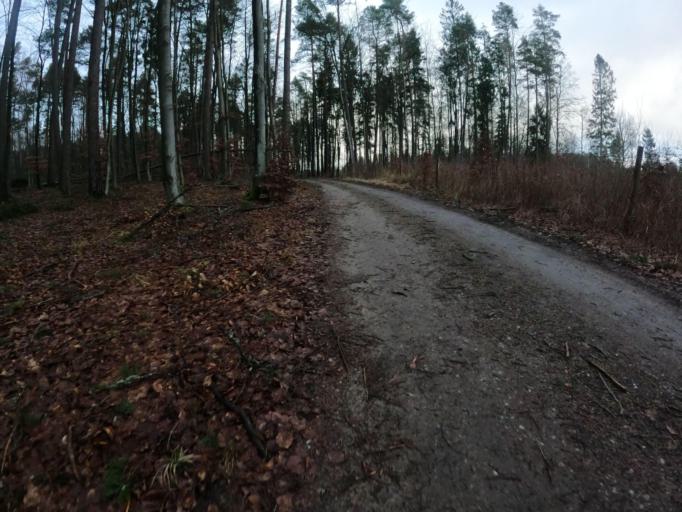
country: PL
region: West Pomeranian Voivodeship
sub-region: Powiat slawienski
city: Slawno
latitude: 54.2752
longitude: 16.7197
